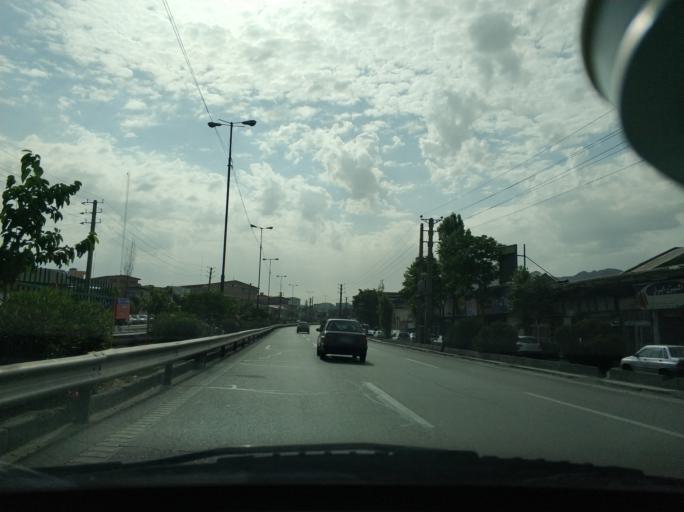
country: IR
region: Tehran
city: Tehran
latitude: 35.7260
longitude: 51.5618
